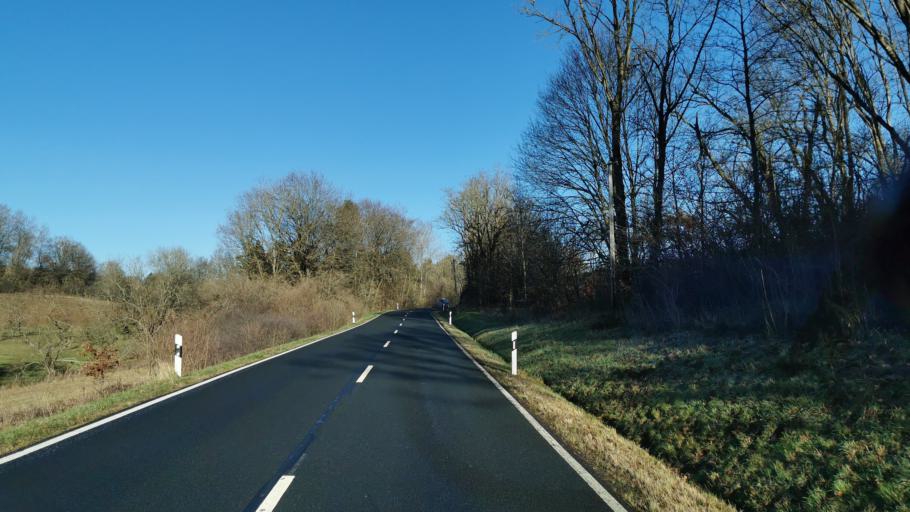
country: DE
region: Rheinland-Pfalz
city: Darscheid
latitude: 50.2156
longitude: 6.8985
